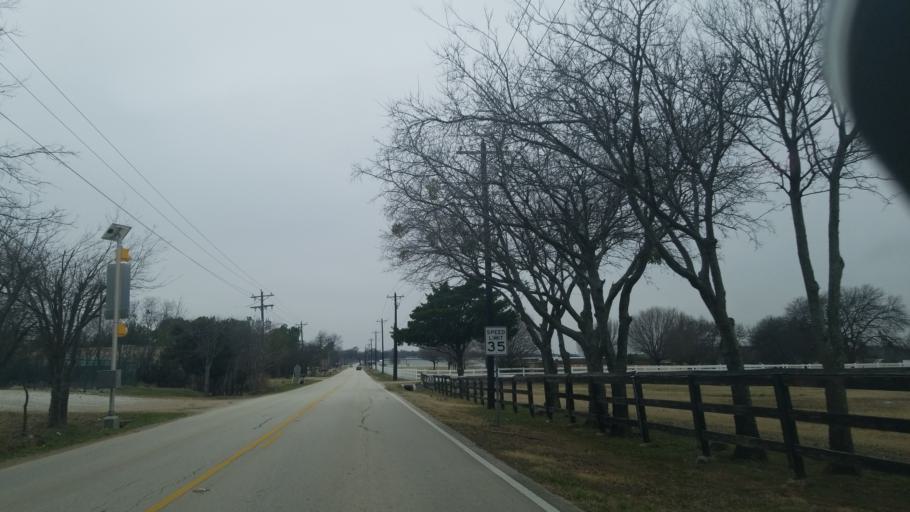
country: US
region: Texas
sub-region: Denton County
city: Copper Canyon
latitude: 33.1177
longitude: -97.1259
